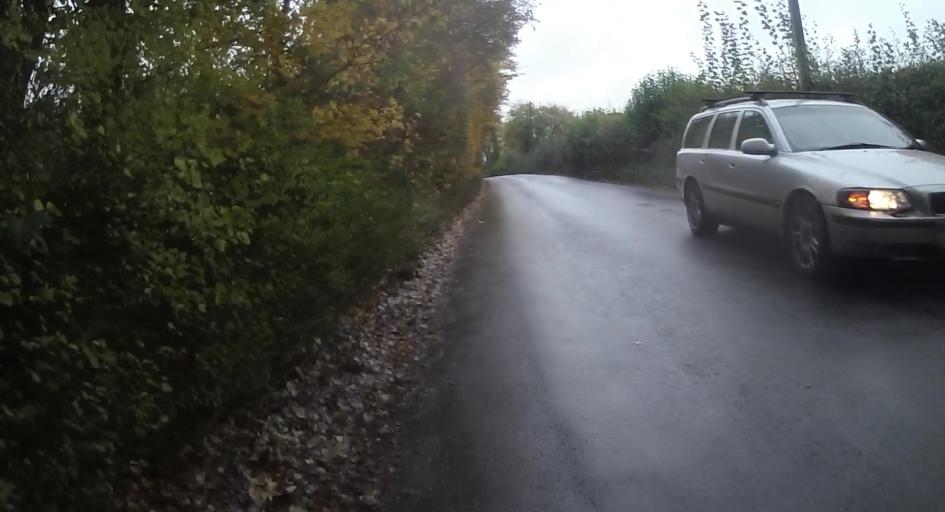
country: GB
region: England
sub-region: Surrey
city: Farnham
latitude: 51.2172
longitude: -0.8393
